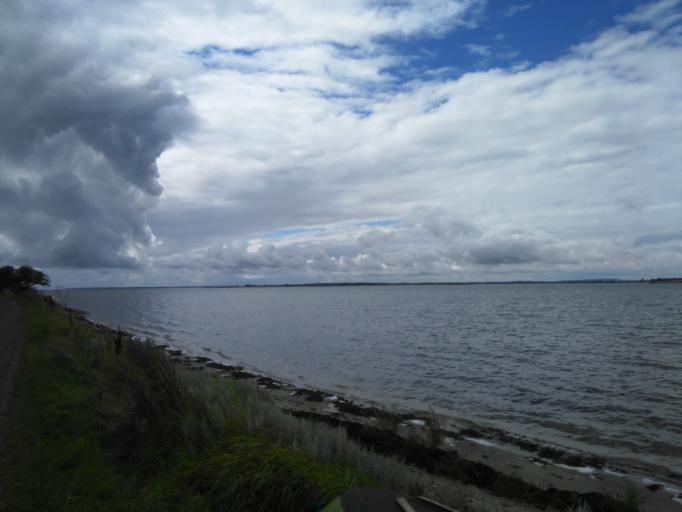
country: DK
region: Central Jutland
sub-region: Odder Kommune
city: Odder
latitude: 55.8639
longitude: 10.1401
